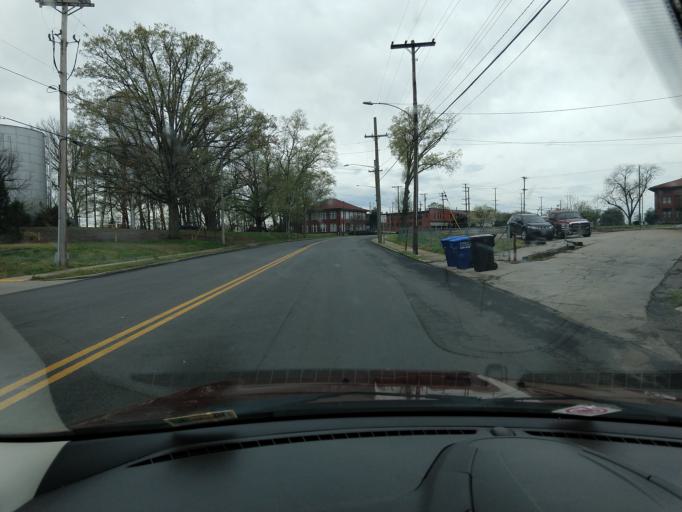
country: US
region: Virginia
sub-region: City of Danville
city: Danville
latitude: 36.5704
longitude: -79.4230
